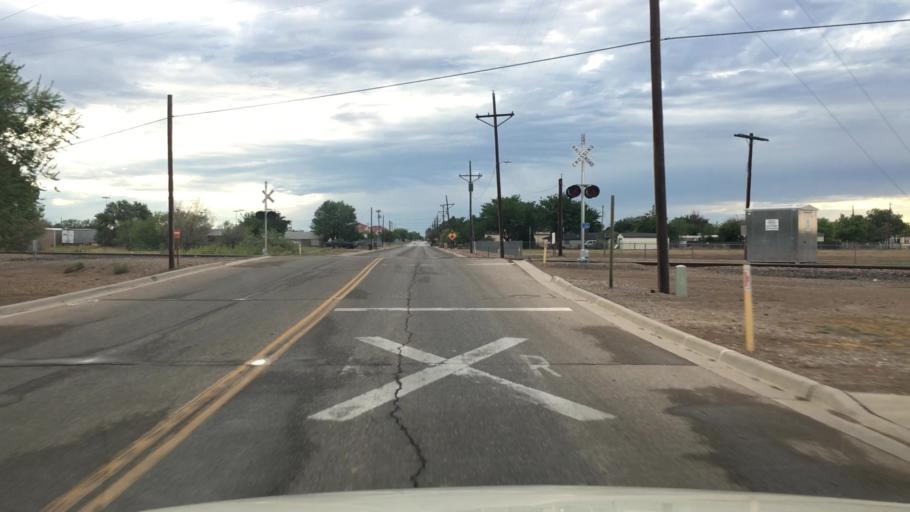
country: US
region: New Mexico
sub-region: Chaves County
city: Roswell
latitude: 33.4160
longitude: -104.5101
